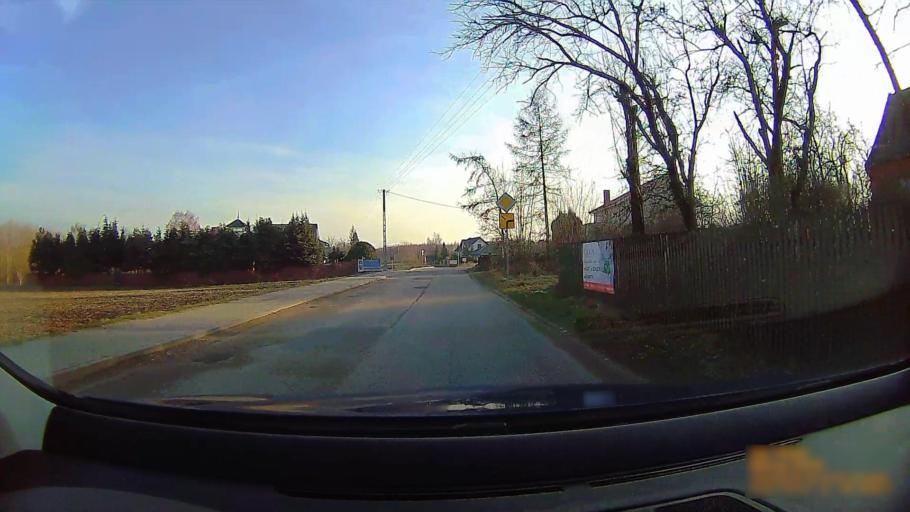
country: PL
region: Greater Poland Voivodeship
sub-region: Konin
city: Konin
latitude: 52.1917
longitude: 18.3056
